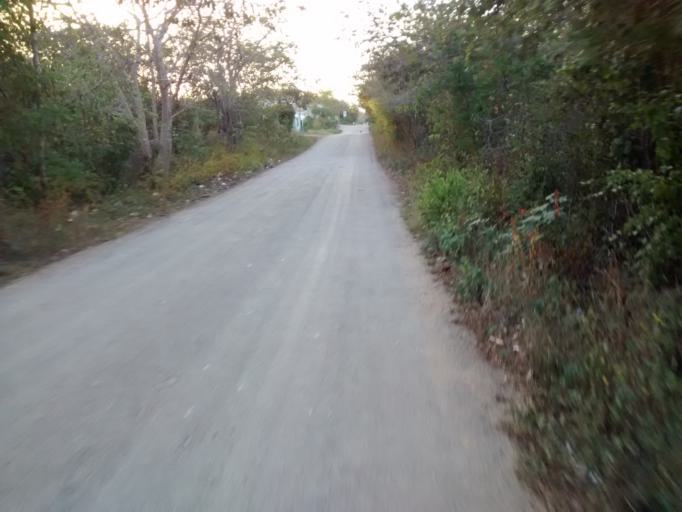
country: MX
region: Yucatan
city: Valladolid
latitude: 20.6840
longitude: -88.1762
